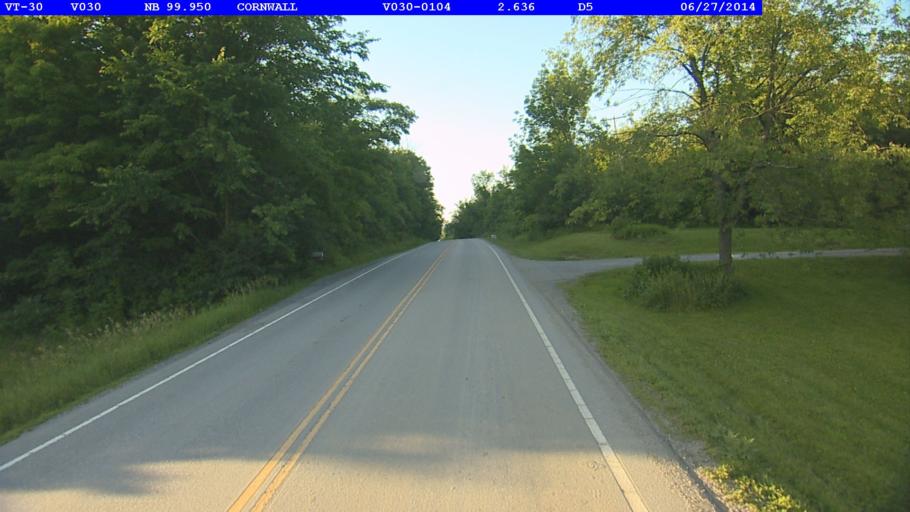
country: US
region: Vermont
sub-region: Addison County
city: Middlebury (village)
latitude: 43.9457
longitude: -73.2112
